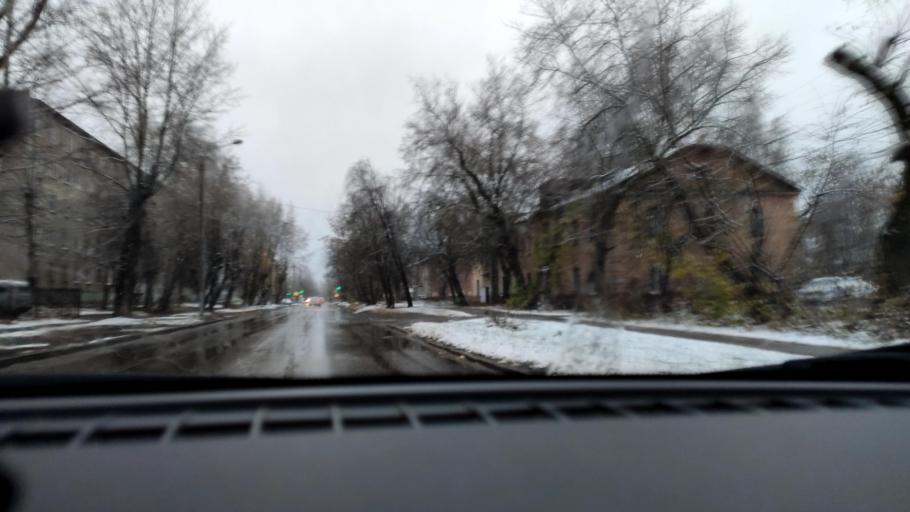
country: RU
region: Perm
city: Kultayevo
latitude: 58.0051
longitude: 55.9462
